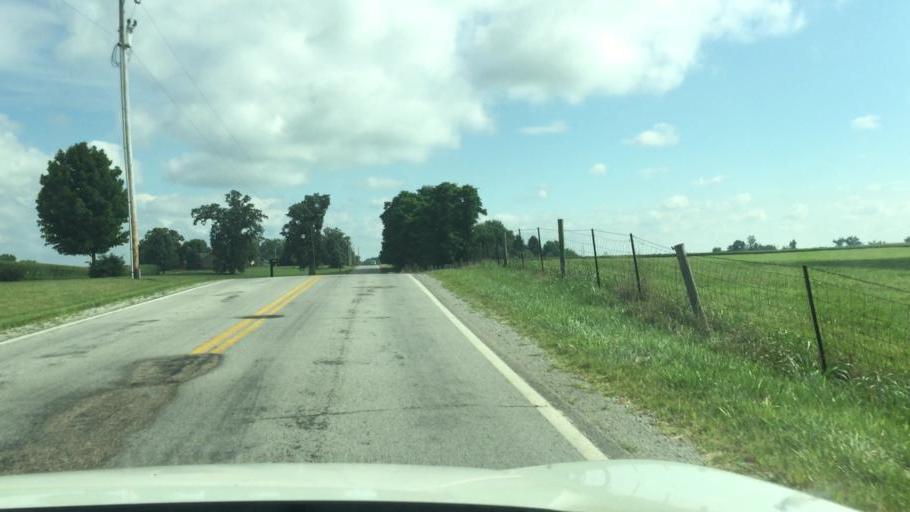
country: US
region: Ohio
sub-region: Clark County
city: Northridge
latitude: 39.9591
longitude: -83.6800
